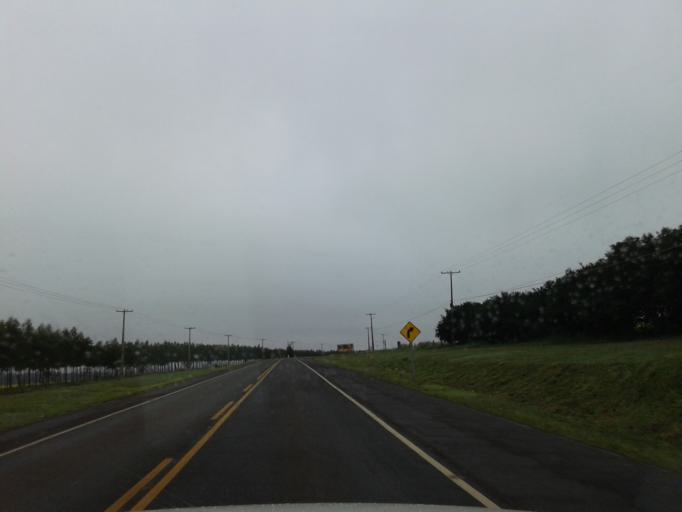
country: PY
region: Alto Parana
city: Naranjal
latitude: -26.1177
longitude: -55.1599
